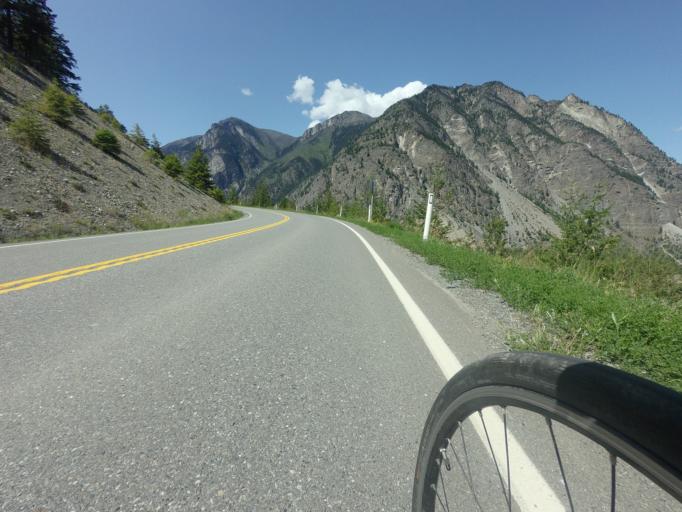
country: CA
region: British Columbia
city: Lillooet
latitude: 50.6618
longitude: -121.9877
